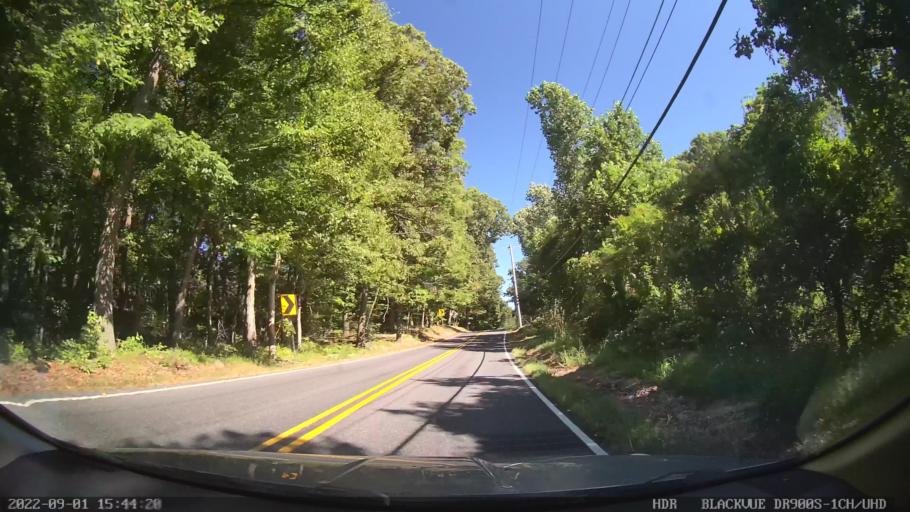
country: US
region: Pennsylvania
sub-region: Berks County
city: Topton
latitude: 40.4732
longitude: -75.6999
